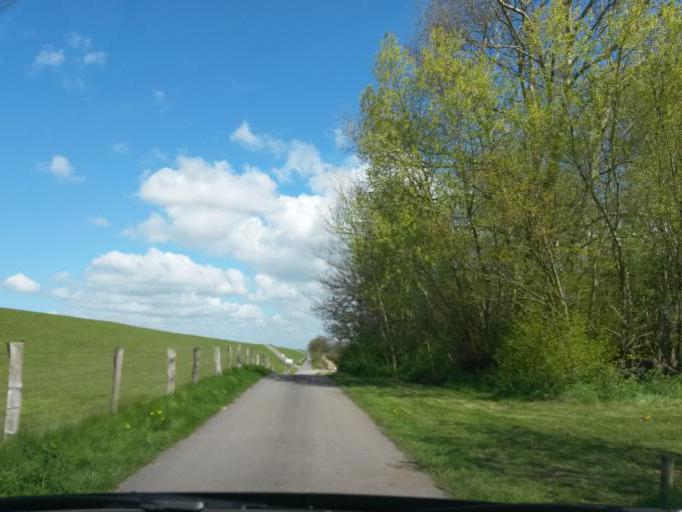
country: DE
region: Schleswig-Holstein
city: Seestermuhe
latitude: 53.6495
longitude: 9.5582
